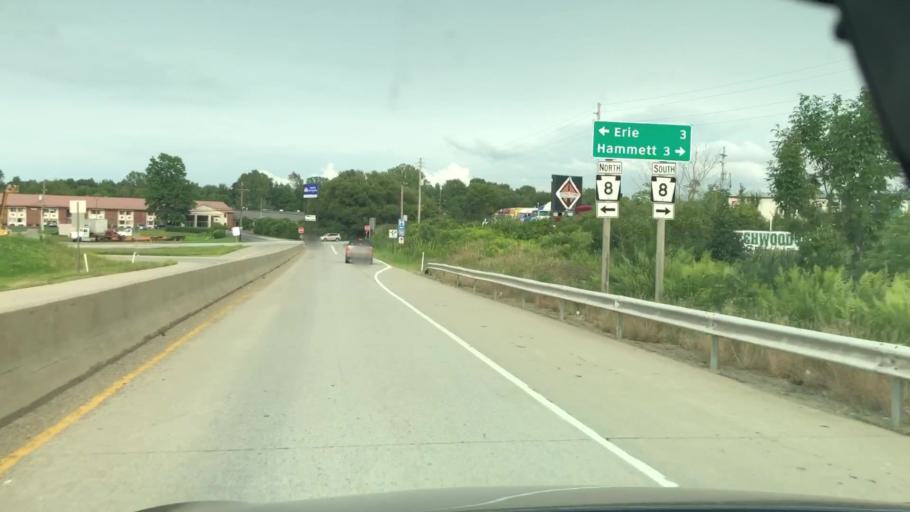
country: US
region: Pennsylvania
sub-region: Erie County
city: Wesleyville
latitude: 42.0920
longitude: -80.0062
